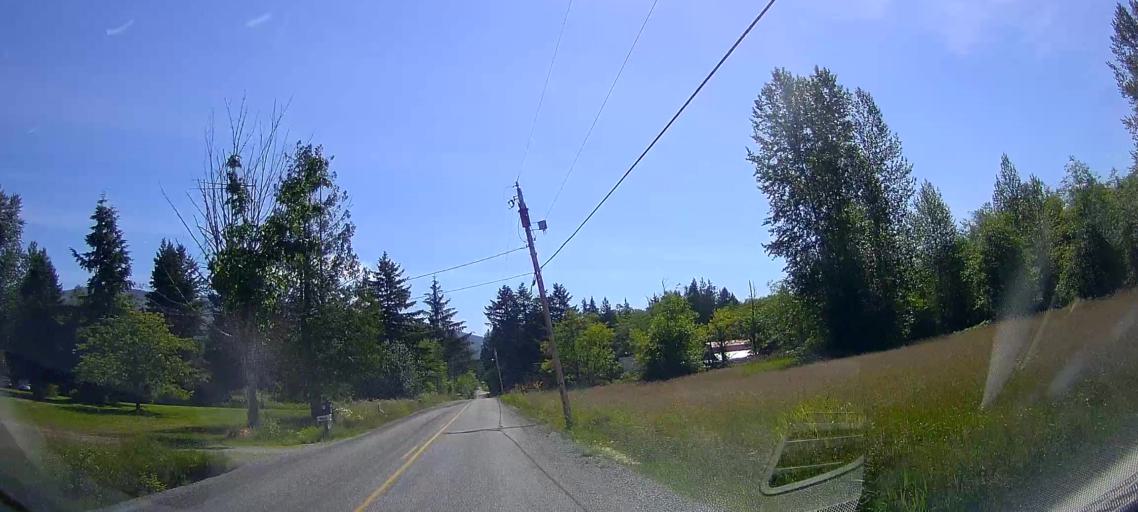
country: US
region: Washington
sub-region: Skagit County
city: Sedro-Woolley
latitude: 48.5578
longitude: -122.2528
